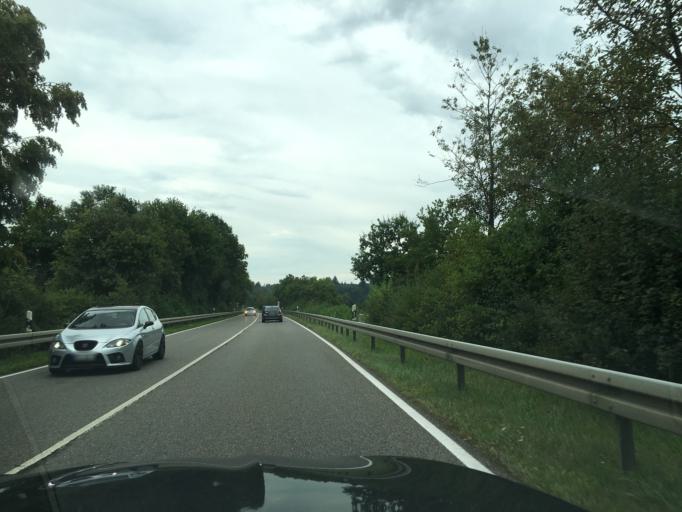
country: DE
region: Baden-Wuerttemberg
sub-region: Freiburg Region
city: Radolfzell am Bodensee
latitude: 47.7699
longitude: 8.9837
